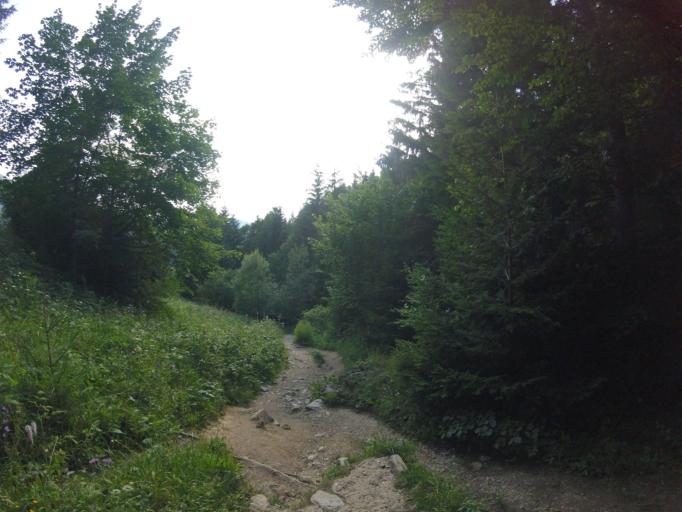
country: SK
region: Zilinsky
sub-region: Okres Zilina
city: Terchova
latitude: 49.2385
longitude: 19.0713
